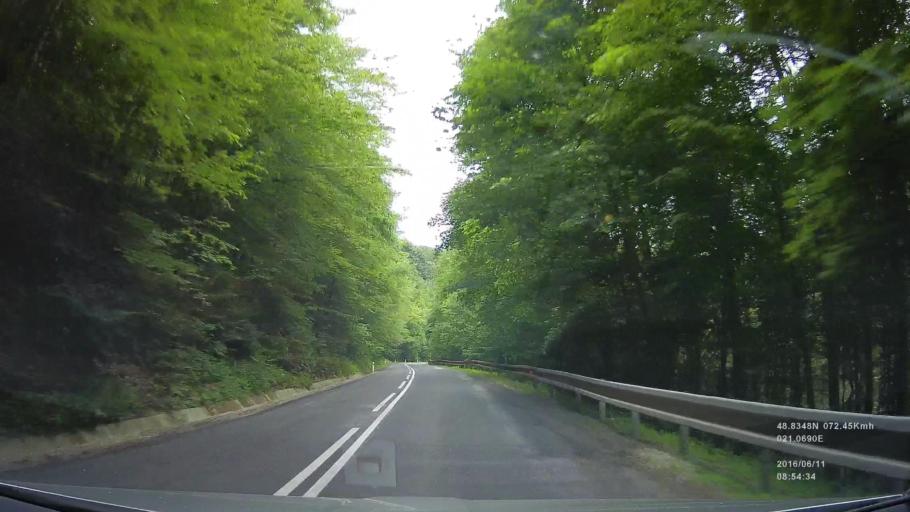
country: SK
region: Kosicky
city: Gelnica
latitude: 48.8328
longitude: 21.0742
